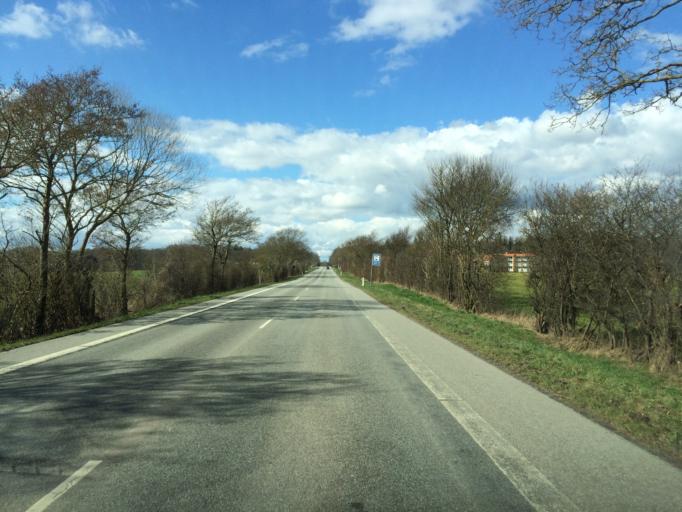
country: DK
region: South Denmark
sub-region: Middelfart Kommune
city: Brenderup
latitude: 55.4420
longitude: 9.9918
